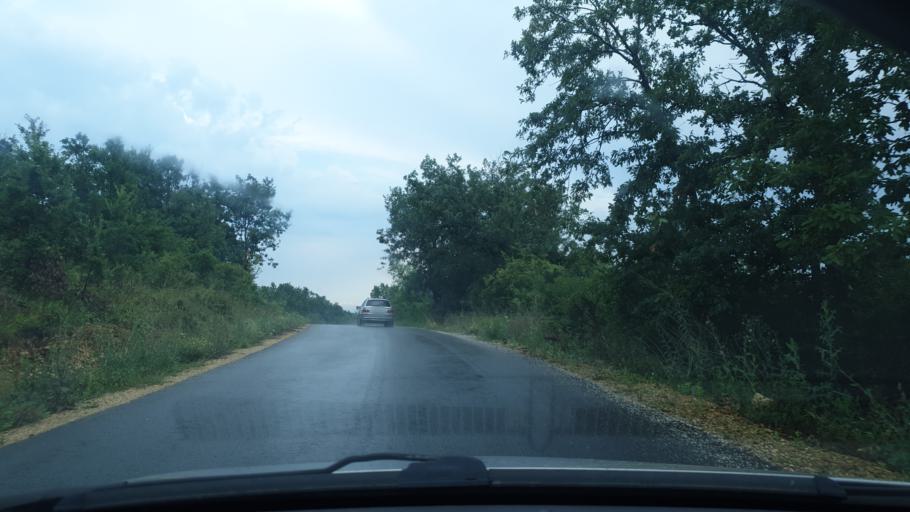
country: RS
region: Central Serbia
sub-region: Sumadijski Okrug
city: Kragujevac
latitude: 44.0561
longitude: 20.7831
